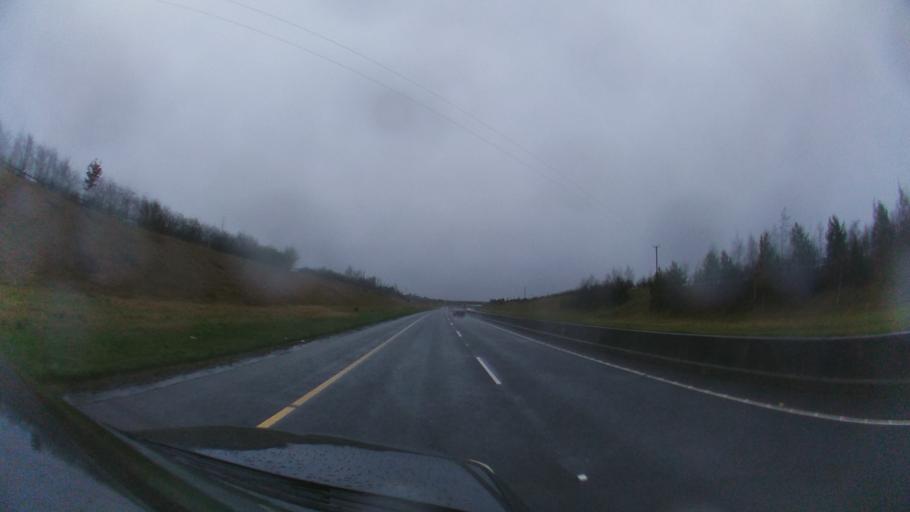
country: IE
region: Leinster
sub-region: Kildare
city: Old Kilcullen
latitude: 53.0674
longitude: -6.7626
